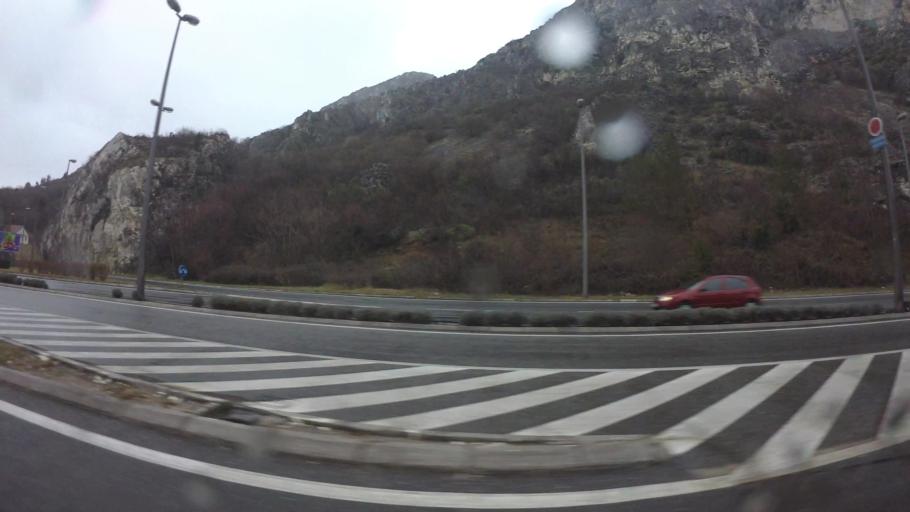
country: BA
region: Federation of Bosnia and Herzegovina
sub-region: Hercegovacko-Bosanski Kanton
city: Mostar
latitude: 43.3277
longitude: 17.8163
